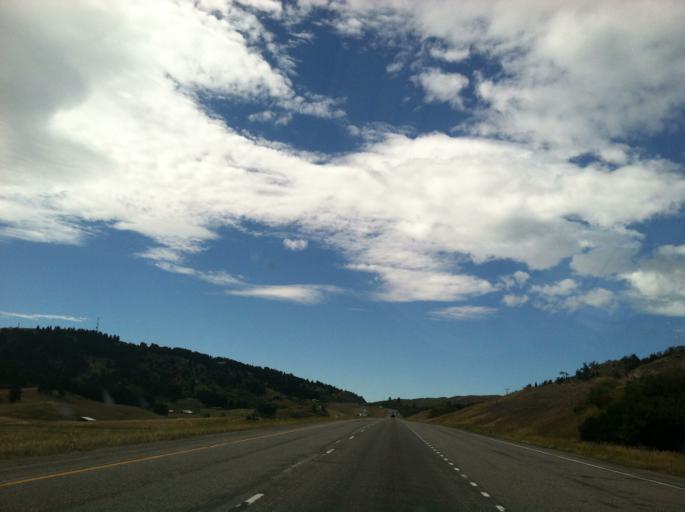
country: US
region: Montana
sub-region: Park County
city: Livingston
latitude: 45.6581
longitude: -110.7810
